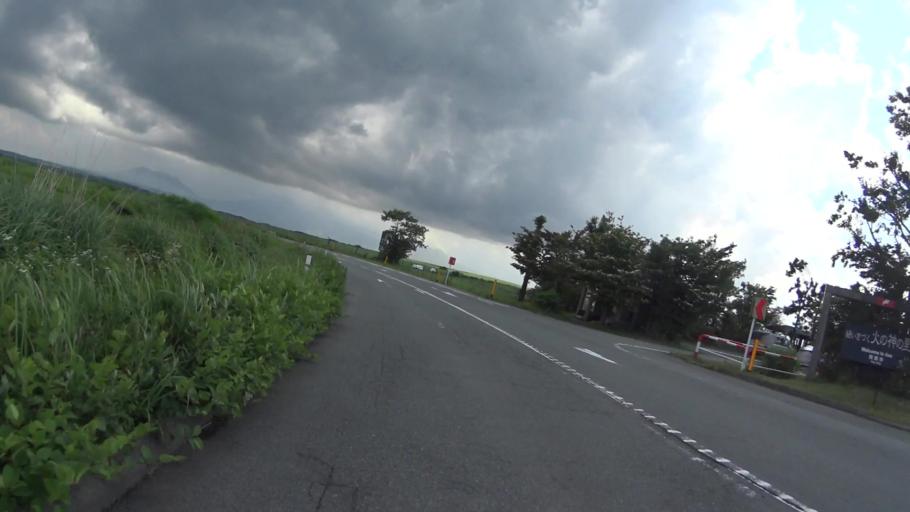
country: JP
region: Kumamoto
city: Aso
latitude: 33.0230
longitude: 131.1512
